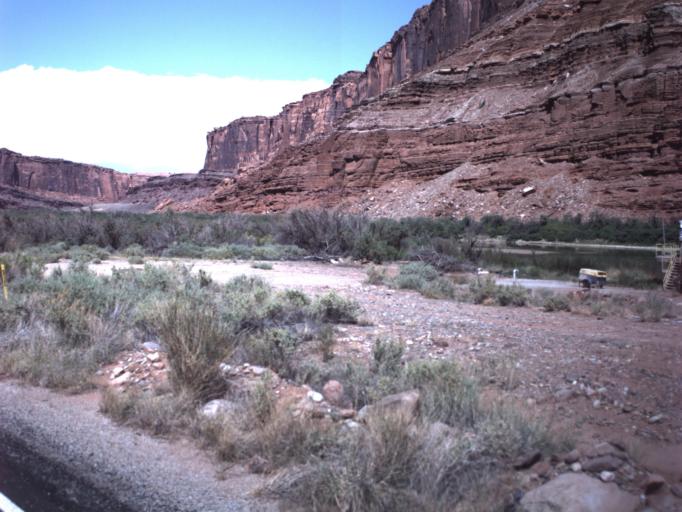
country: US
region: Utah
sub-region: Grand County
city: Moab
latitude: 38.5245
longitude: -109.6544
